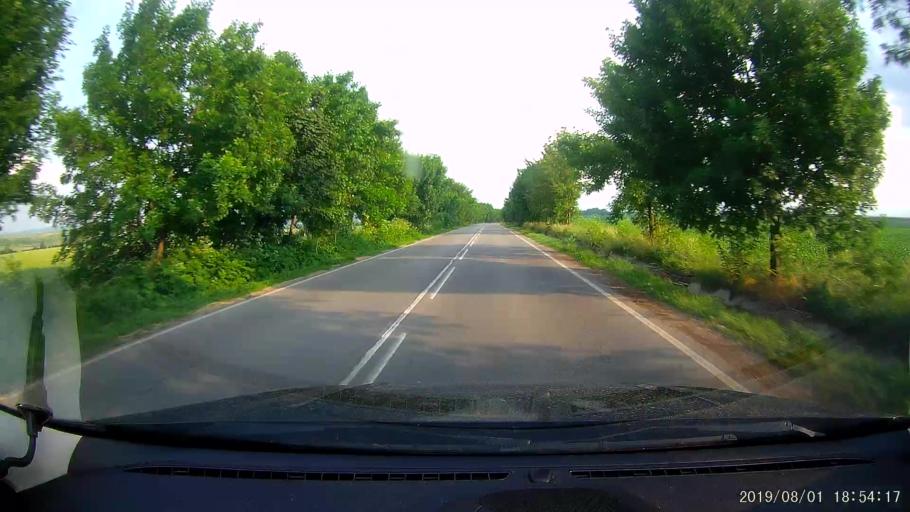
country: BG
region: Shumen
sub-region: Obshtina Shumen
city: Shumen
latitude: 43.2022
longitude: 27.0009
